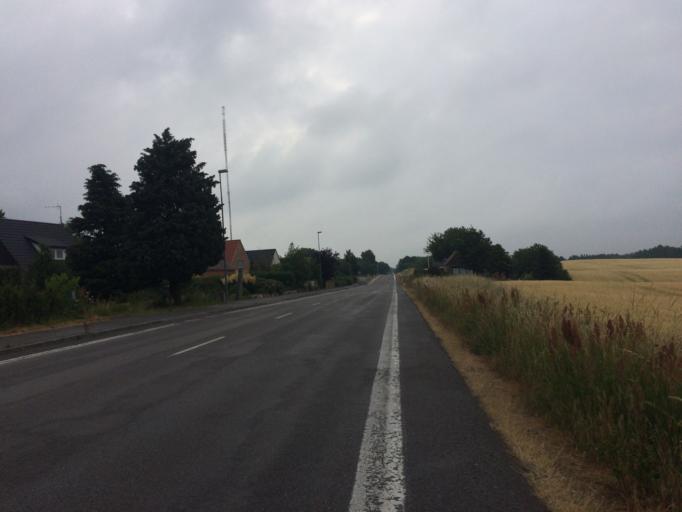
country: DK
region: Capital Region
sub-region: Bornholm Kommune
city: Akirkeby
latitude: 55.1452
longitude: 14.8735
